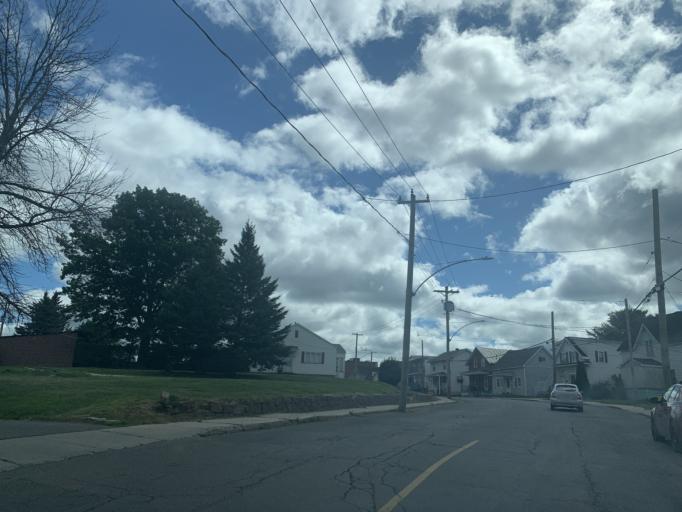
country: CA
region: Ontario
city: Hawkesbury
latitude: 45.6084
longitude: -74.6120
